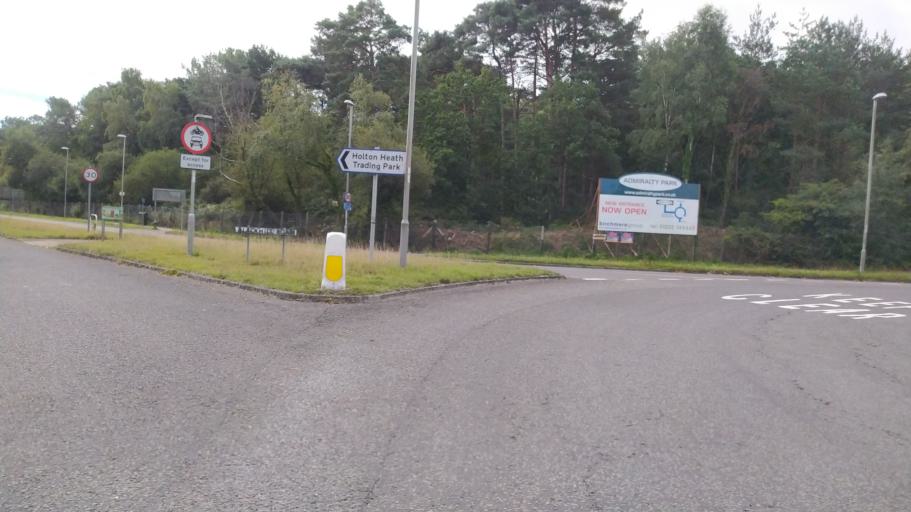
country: GB
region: England
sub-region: Dorset
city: Lytchett Matravers
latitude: 50.7222
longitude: -2.0798
